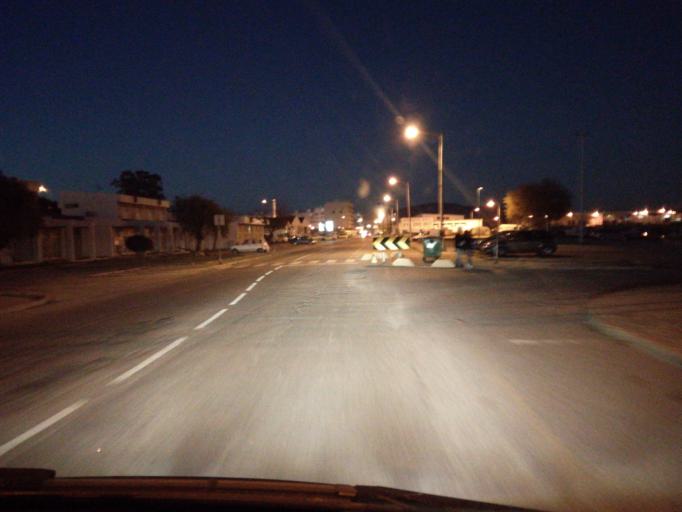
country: PT
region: Faro
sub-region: Olhao
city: Olhao
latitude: 37.0250
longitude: -7.8362
